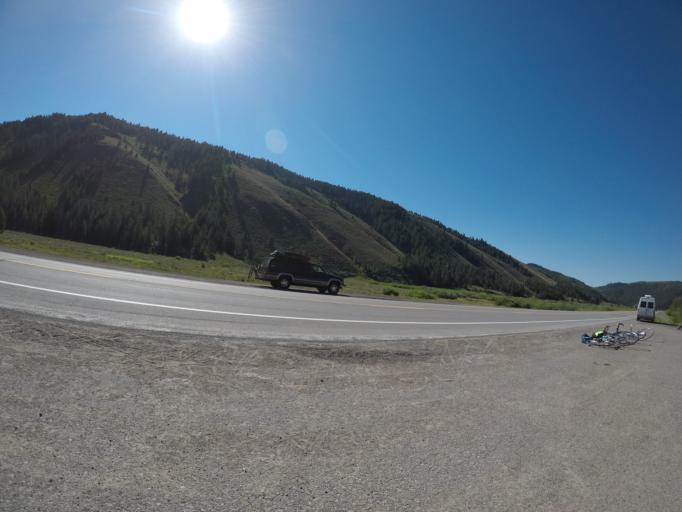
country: US
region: Wyoming
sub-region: Lincoln County
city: Afton
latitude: 42.4827
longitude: -110.9628
